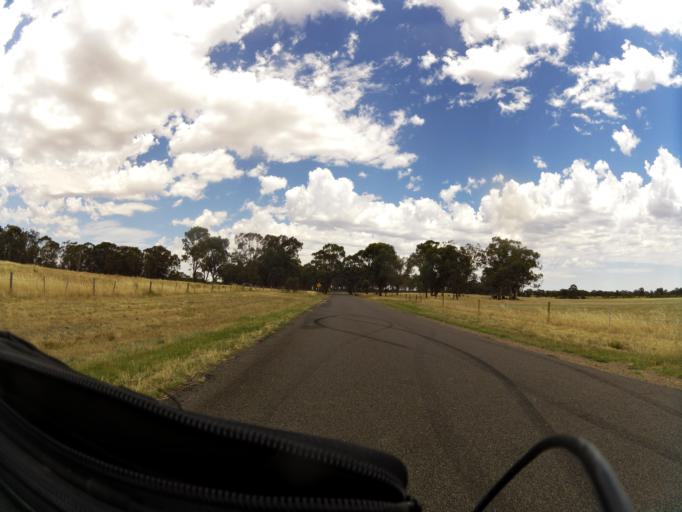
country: AU
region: Victoria
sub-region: Greater Shepparton
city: Shepparton
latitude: -36.7017
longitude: 145.1686
